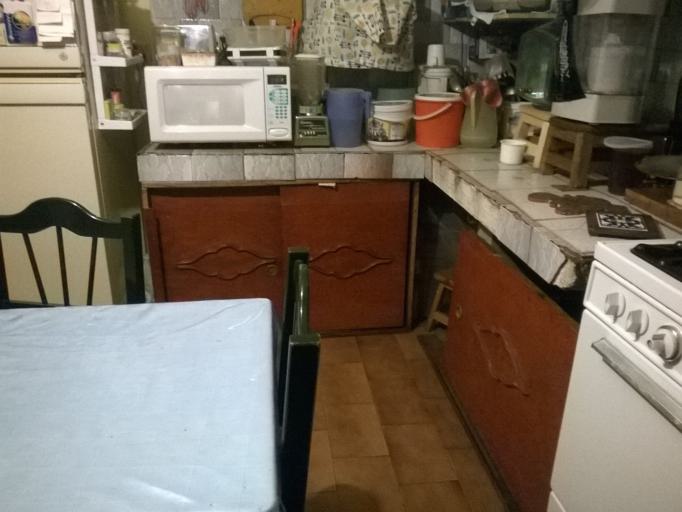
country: MX
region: Mexico
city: Toluca
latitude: 19.2702
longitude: -99.6444
